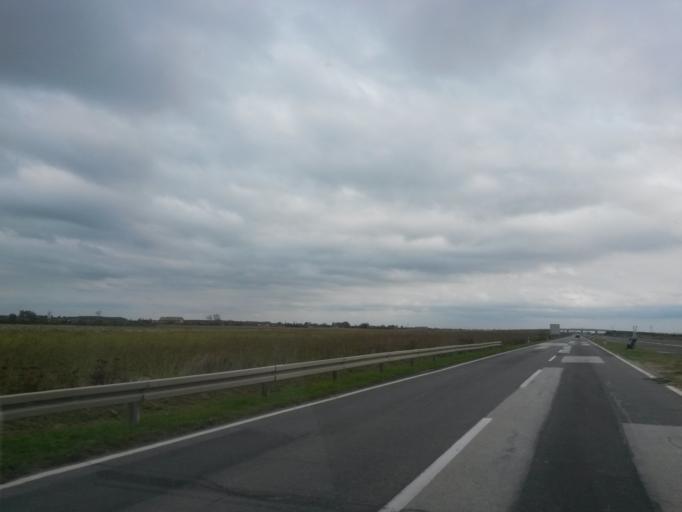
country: HR
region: Osjecko-Baranjska
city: Josipovac
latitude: 45.5685
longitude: 18.5838
